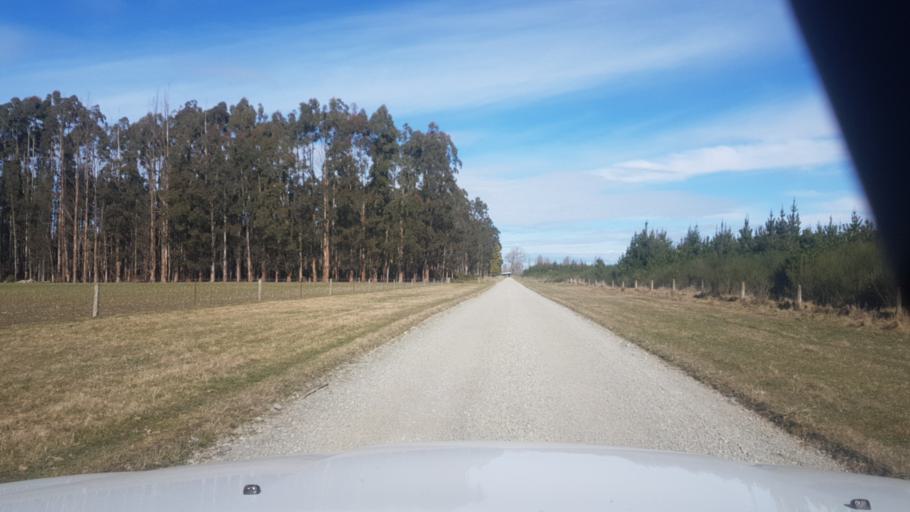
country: NZ
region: Canterbury
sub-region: Timaru District
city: Pleasant Point
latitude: -44.1391
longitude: 171.2762
